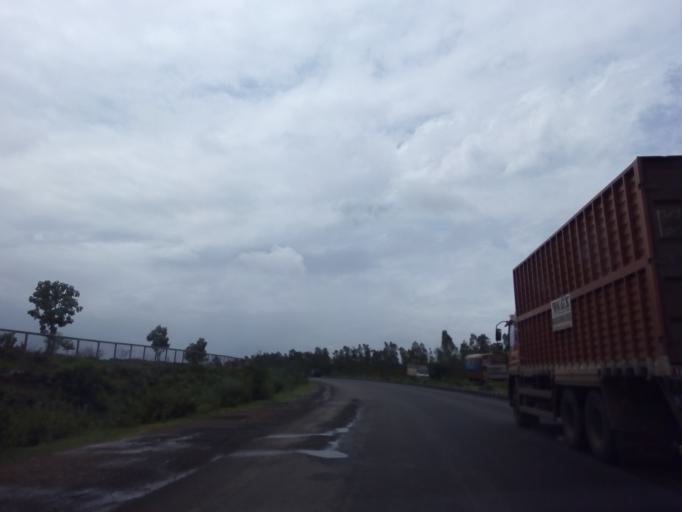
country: IN
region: Karnataka
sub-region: Haveri
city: Byadgi
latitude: 14.7123
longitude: 75.5037
